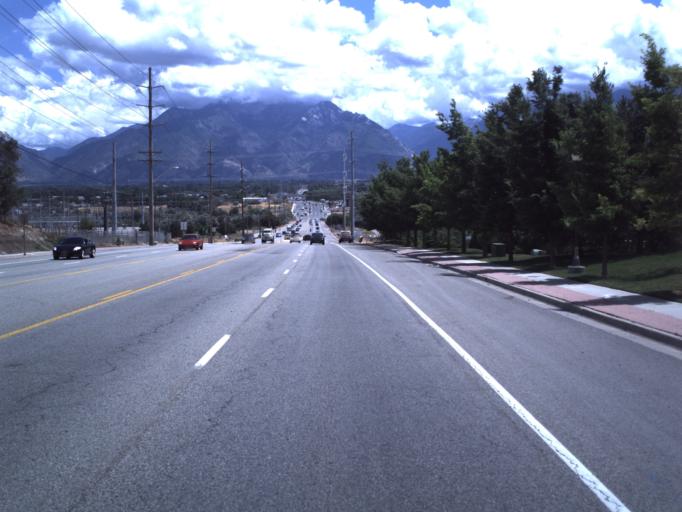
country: US
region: Utah
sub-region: Salt Lake County
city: South Jordan
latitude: 40.5877
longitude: -111.9214
